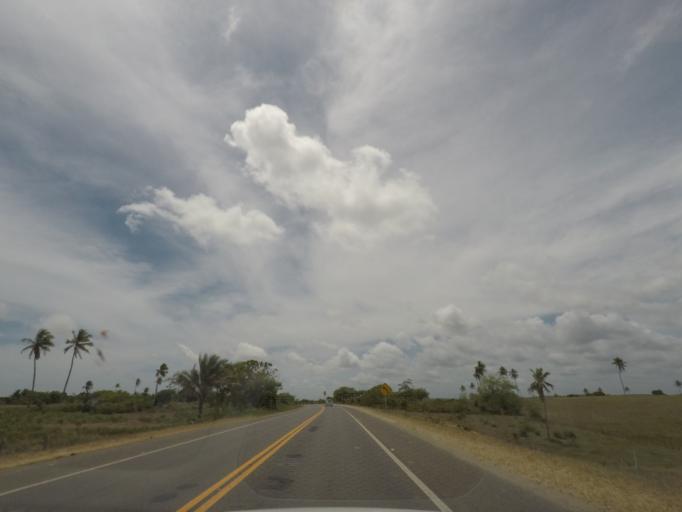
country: BR
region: Bahia
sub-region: Conde
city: Conde
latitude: -11.8132
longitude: -37.6341
